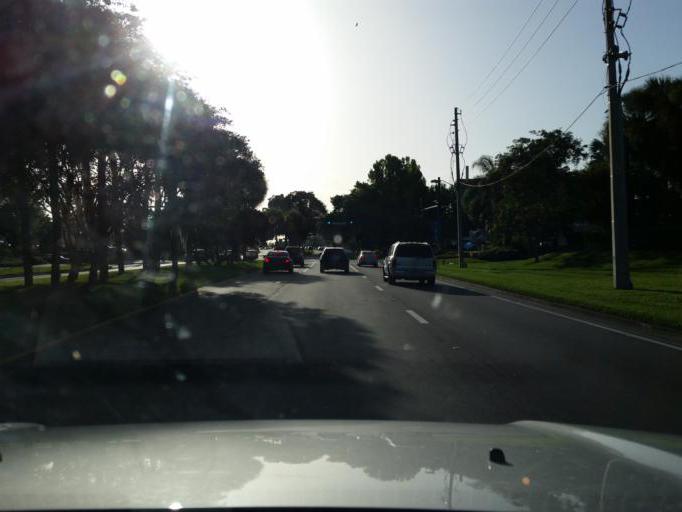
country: US
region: Florida
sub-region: Orange County
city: Williamsburg
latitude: 28.4077
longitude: -81.4681
